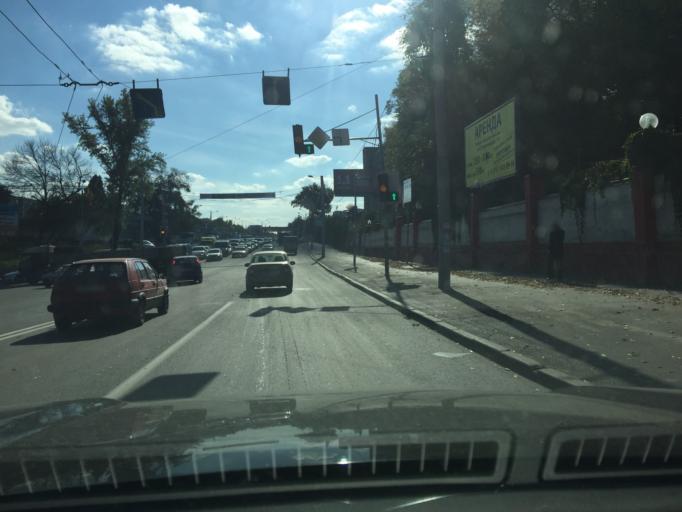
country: RU
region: Rostov
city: Imeni Chkalova
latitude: 47.2573
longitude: 39.7651
